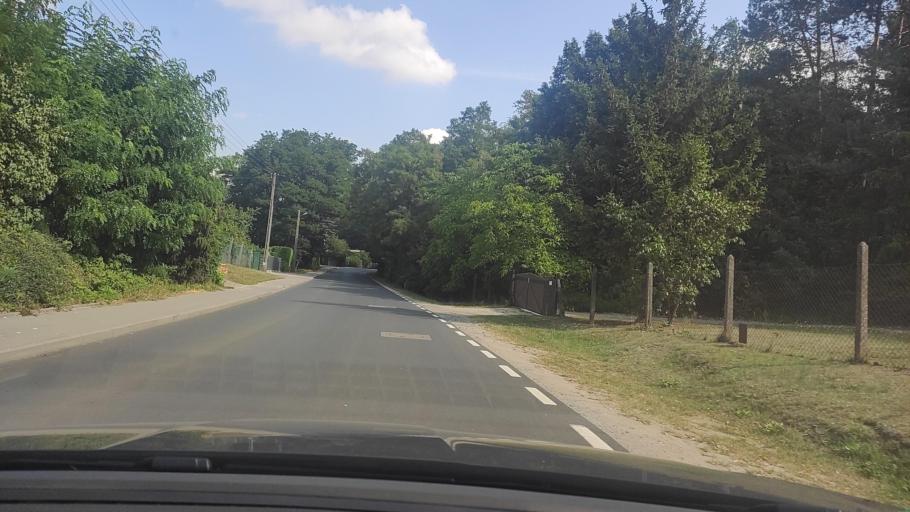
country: PL
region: Greater Poland Voivodeship
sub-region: Powiat poznanski
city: Kostrzyn
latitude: 52.4710
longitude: 17.1791
